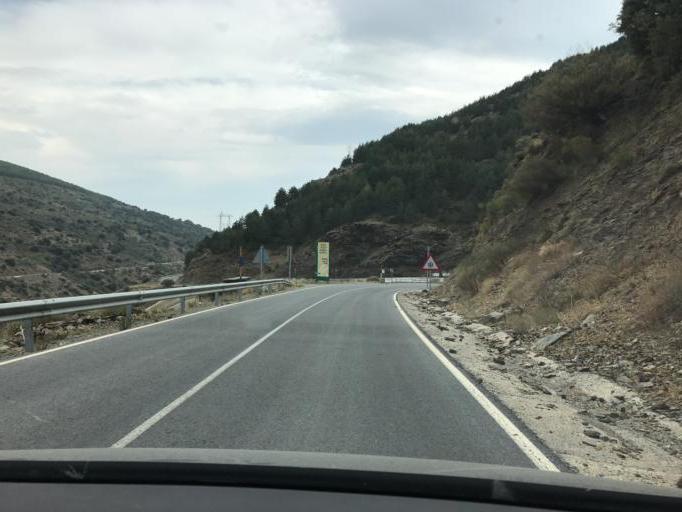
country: ES
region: Andalusia
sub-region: Provincia de Almeria
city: Bayarcal
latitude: 37.0748
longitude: -3.0209
